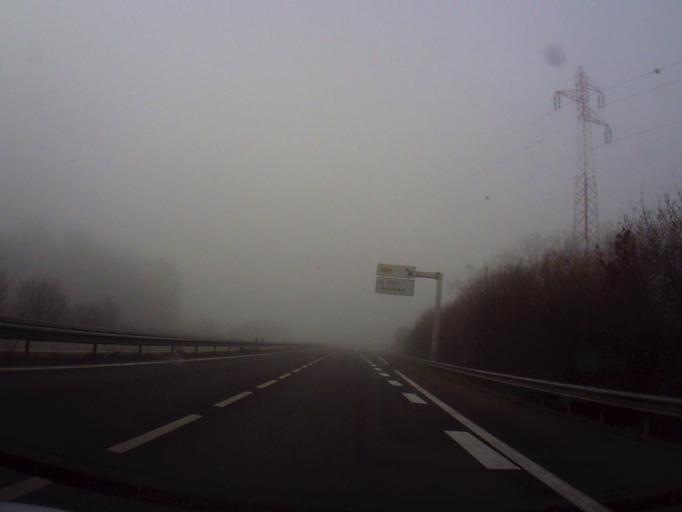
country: FR
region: Brittany
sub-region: Departement d'Ille-et-Vilaine
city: Le Rheu
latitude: 48.0829
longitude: -1.7886
